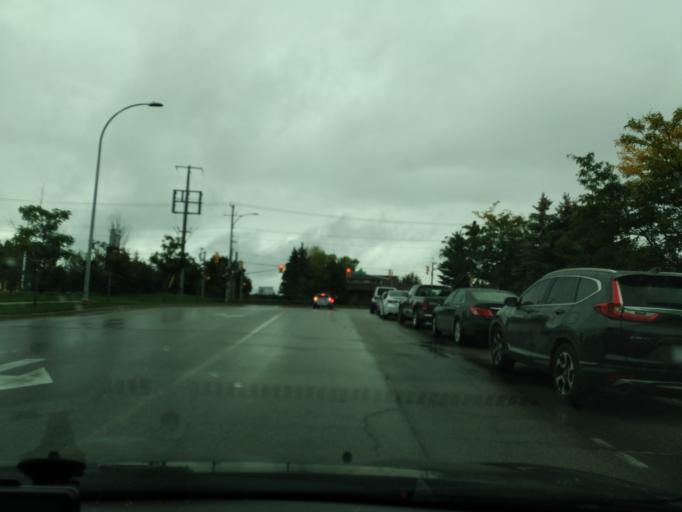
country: CA
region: Ontario
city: Barrie
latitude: 44.4158
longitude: -79.6591
